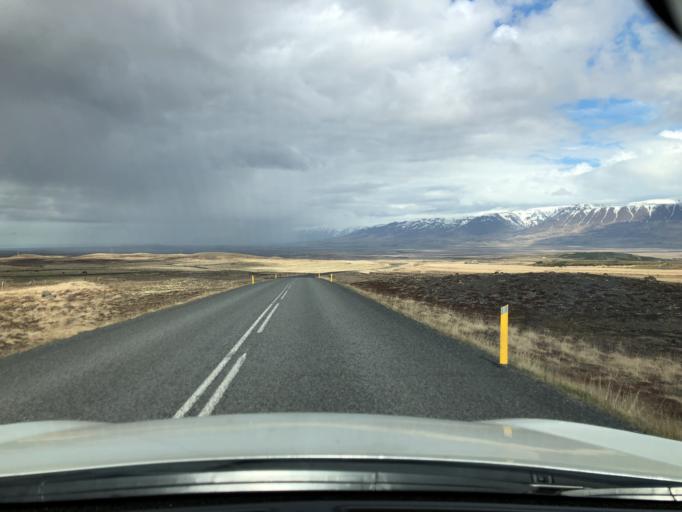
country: IS
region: Northwest
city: Saudarkrokur
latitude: 65.5333
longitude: -19.5122
